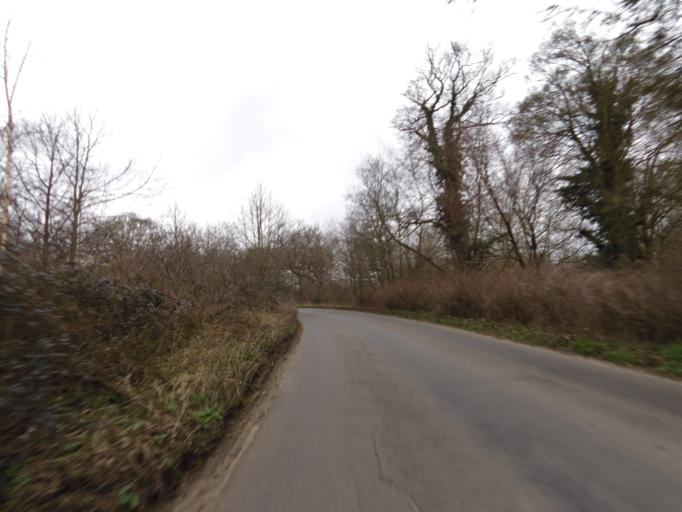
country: GB
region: England
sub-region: Suffolk
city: Wickham Market
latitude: 52.1631
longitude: 1.3565
